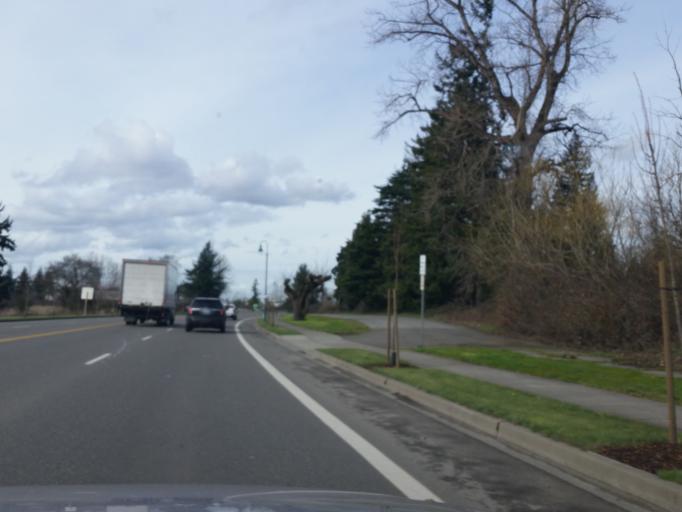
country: US
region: Washington
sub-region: Pierce County
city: Milton
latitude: 47.2218
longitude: -122.3234
